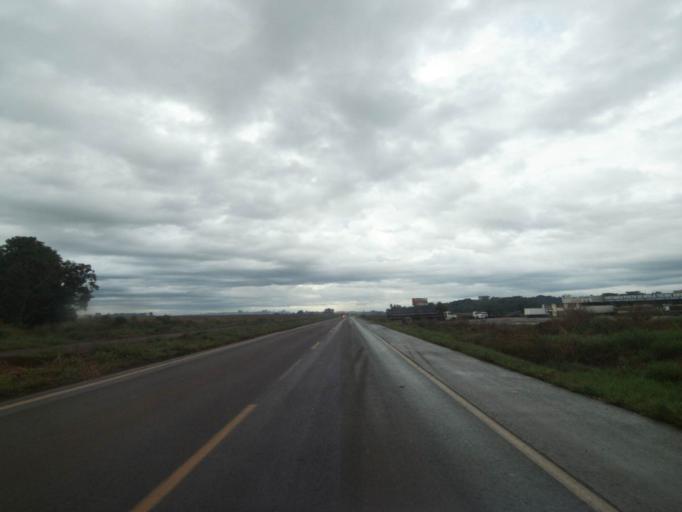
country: BR
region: Parana
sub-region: Toledo
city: Toledo
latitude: -24.7013
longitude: -53.7316
